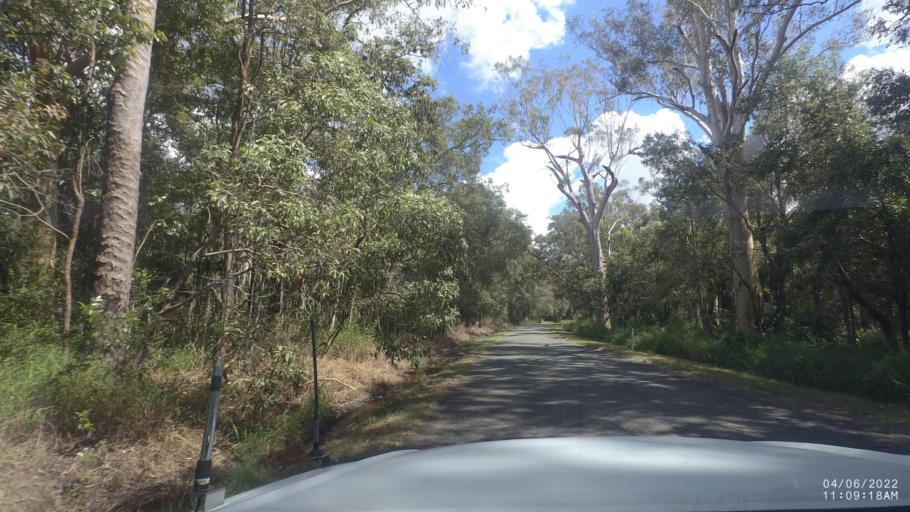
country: AU
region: Queensland
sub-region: Logan
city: Chambers Flat
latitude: -27.7754
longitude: 153.0748
